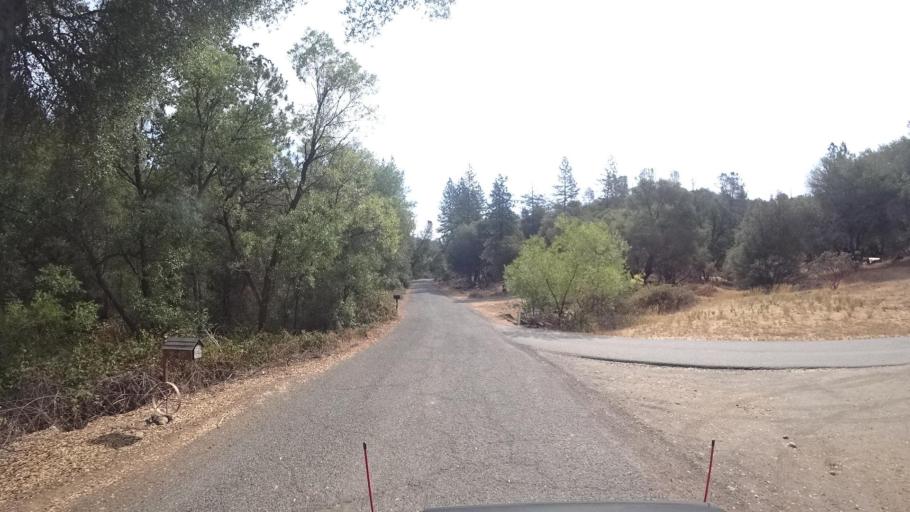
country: US
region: California
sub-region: Mariposa County
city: Midpines
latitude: 37.5626
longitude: -119.9758
